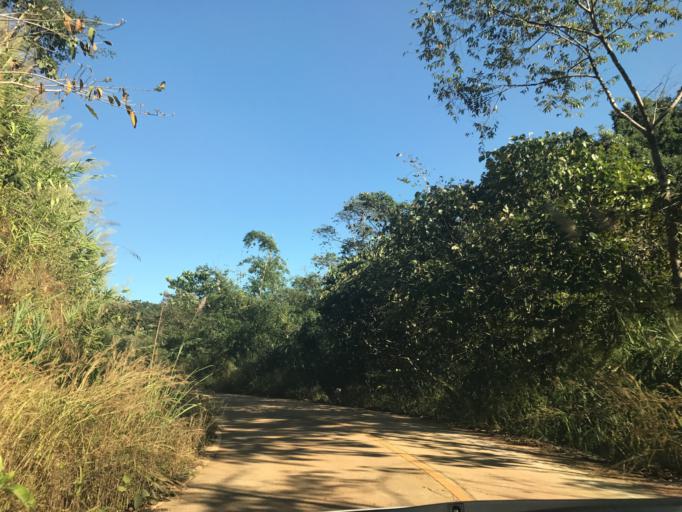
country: TH
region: Tak
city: Phop Phra
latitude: 16.5684
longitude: 98.8260
